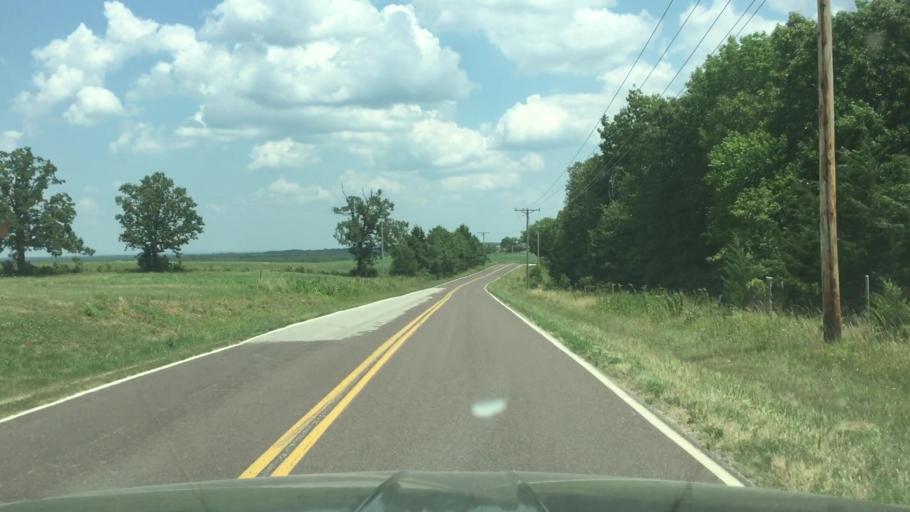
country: US
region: Missouri
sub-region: Miller County
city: Tuscumbia
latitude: 38.1193
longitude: -92.4704
